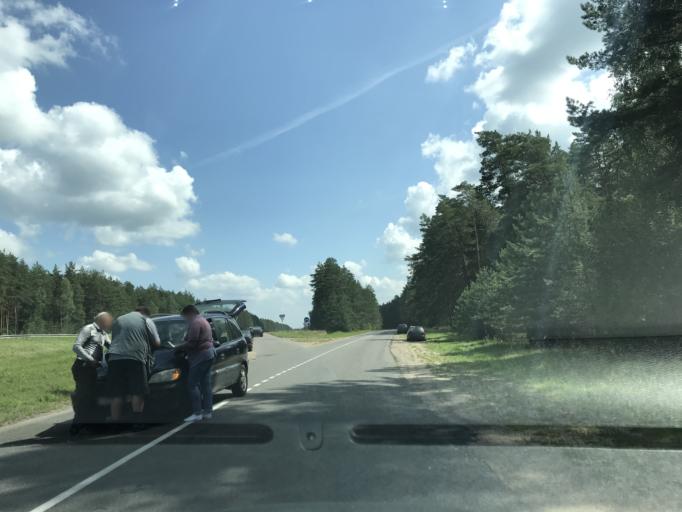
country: BY
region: Minsk
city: Rakaw
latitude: 53.9829
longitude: 27.0010
